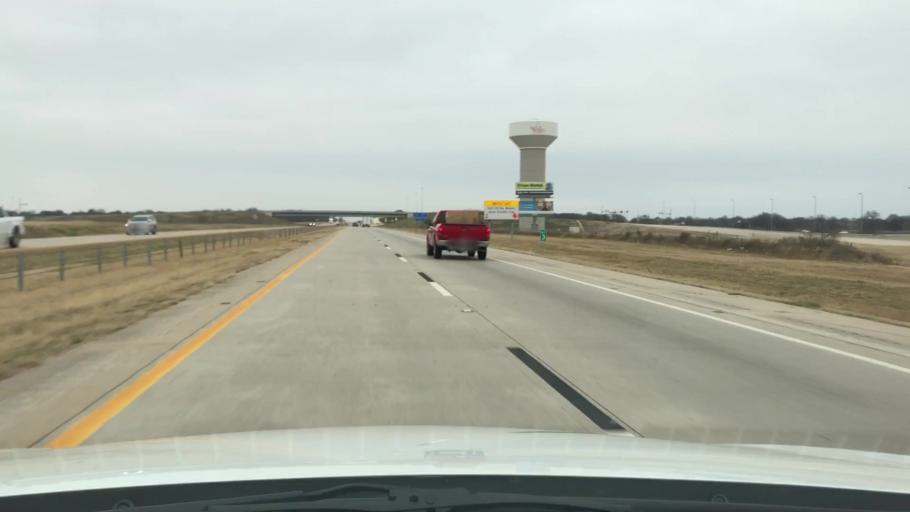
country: US
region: Texas
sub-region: Cooke County
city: Gainesville
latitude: 33.7619
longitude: -97.1348
